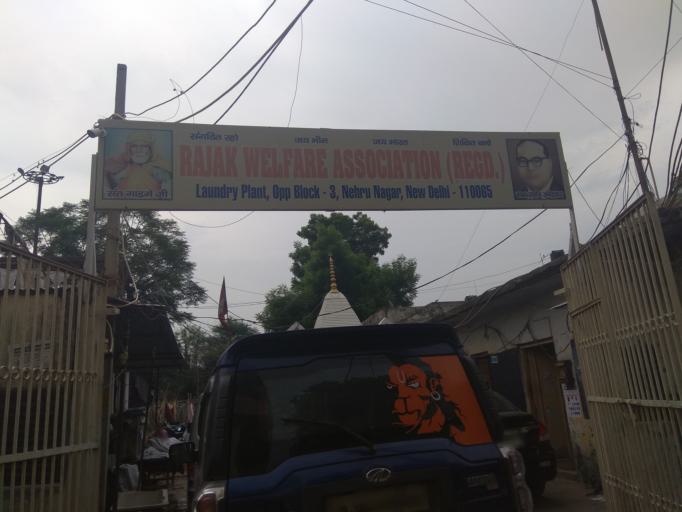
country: IN
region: NCT
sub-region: New Delhi
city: New Delhi
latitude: 28.5715
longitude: 77.2543
